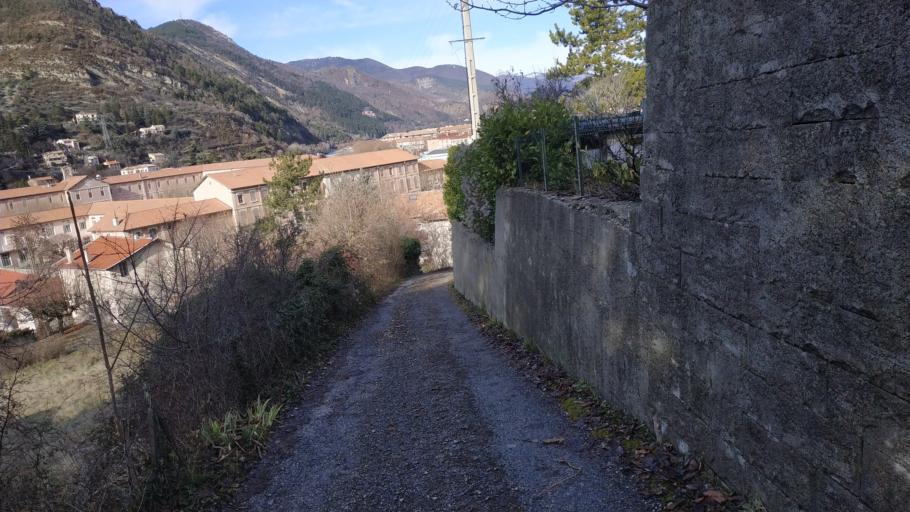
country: FR
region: Provence-Alpes-Cote d'Azur
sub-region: Departement des Alpes-de-Haute-Provence
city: Digne-les-Bains
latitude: 44.0876
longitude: 6.2323
